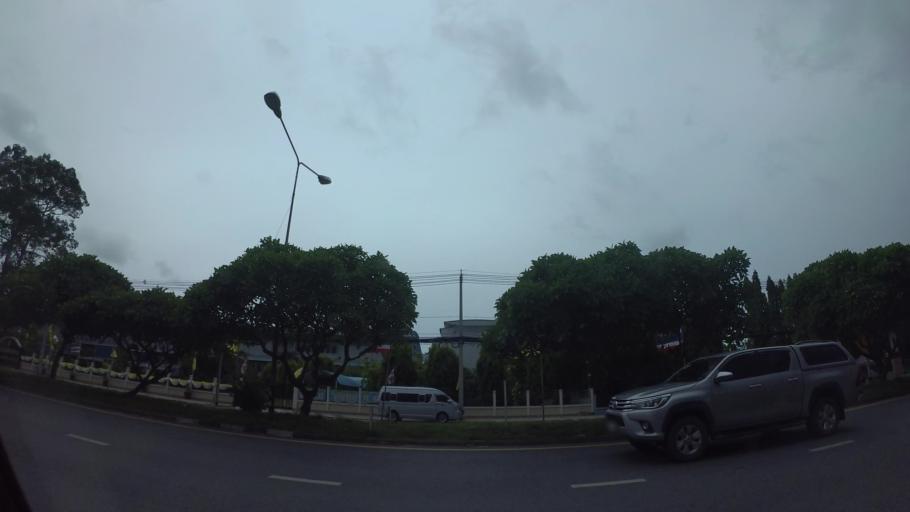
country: TH
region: Rayong
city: Rayong
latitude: 12.6884
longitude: 101.2630
